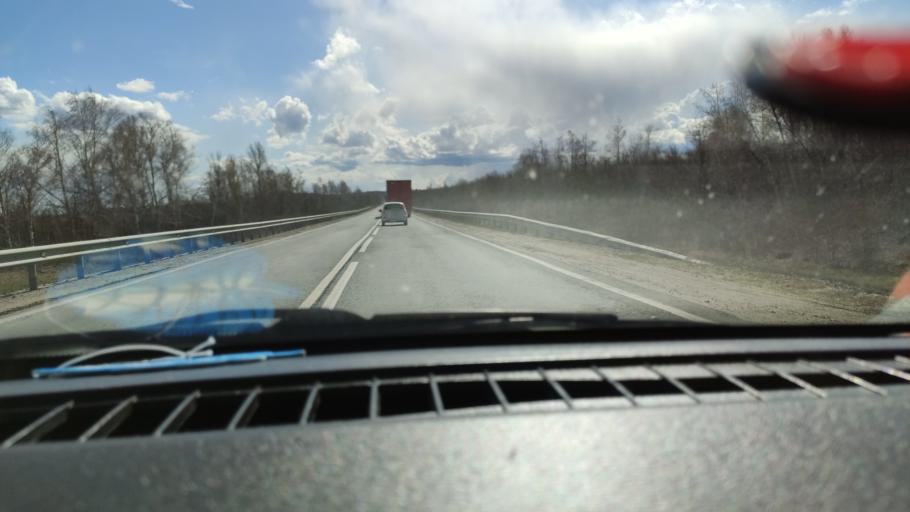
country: RU
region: Saratov
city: Dukhovnitskoye
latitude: 52.6749
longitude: 48.2261
